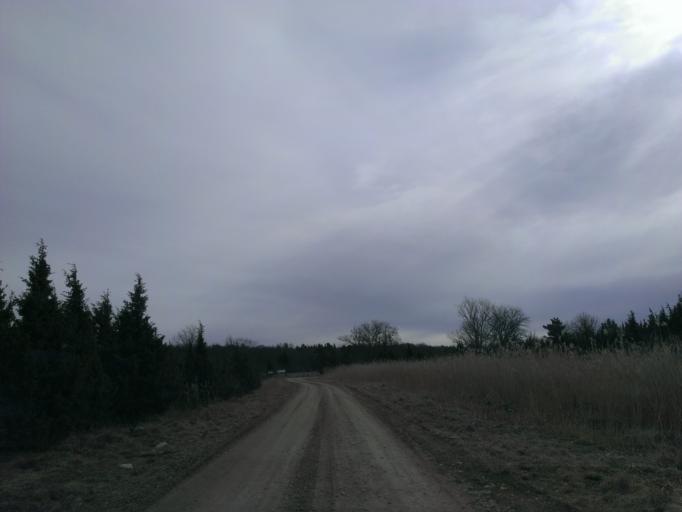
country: EE
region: Laeaene
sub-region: Lihula vald
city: Lihula
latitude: 58.5644
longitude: 23.5483
